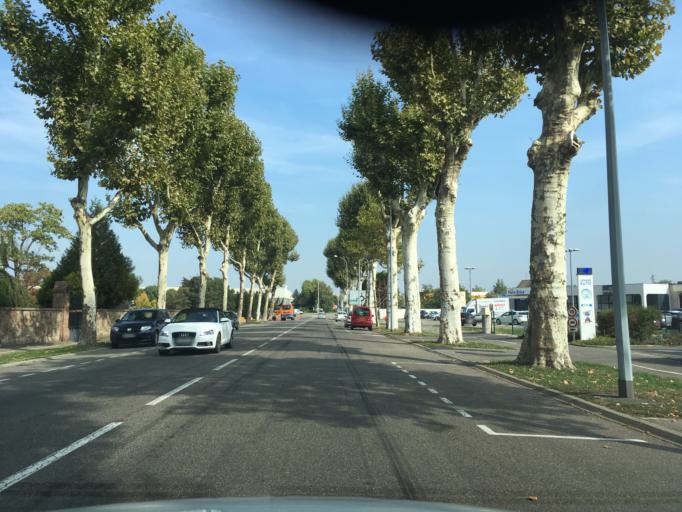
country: FR
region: Alsace
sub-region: Departement du Haut-Rhin
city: Colmar
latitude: 48.0938
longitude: 7.3732
